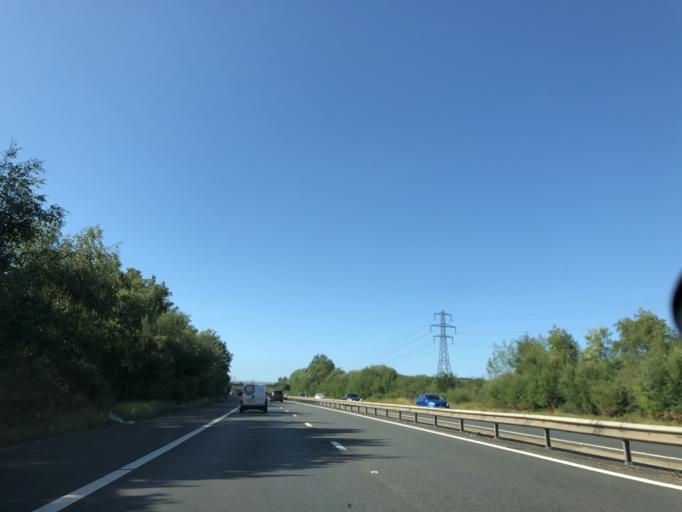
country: GB
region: England
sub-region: Hampshire
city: Cowplain
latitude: 50.8975
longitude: -0.9987
